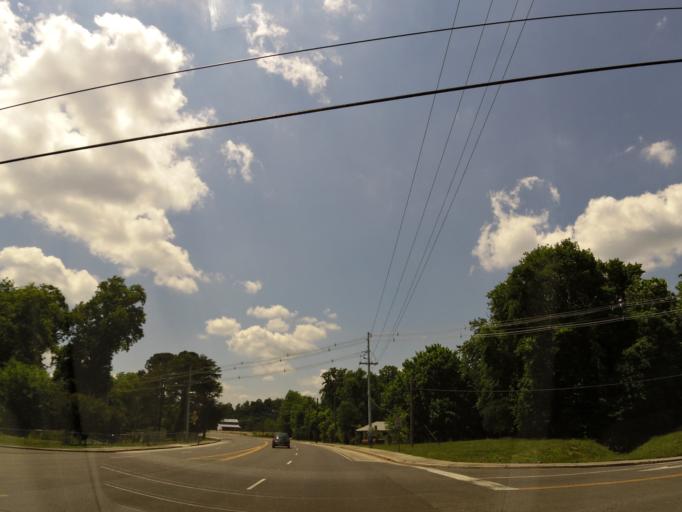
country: US
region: Tennessee
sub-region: Rhea County
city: Dayton
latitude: 35.4987
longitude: -85.0133
